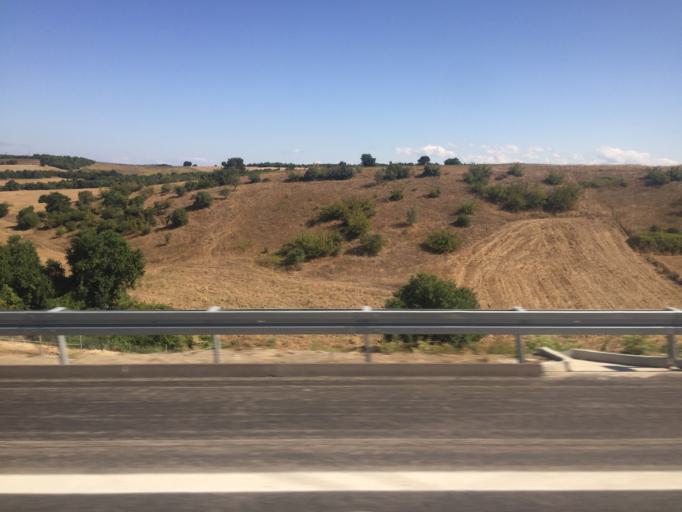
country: TR
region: Bursa
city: Mahmudiye
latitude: 40.2603
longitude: 28.6807
